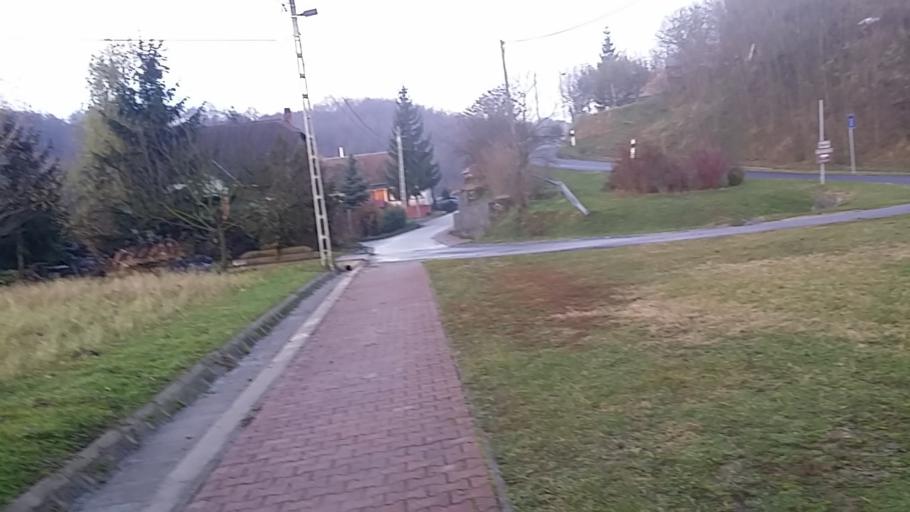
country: HU
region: Tolna
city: Bonyhad
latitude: 46.2268
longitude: 18.6079
